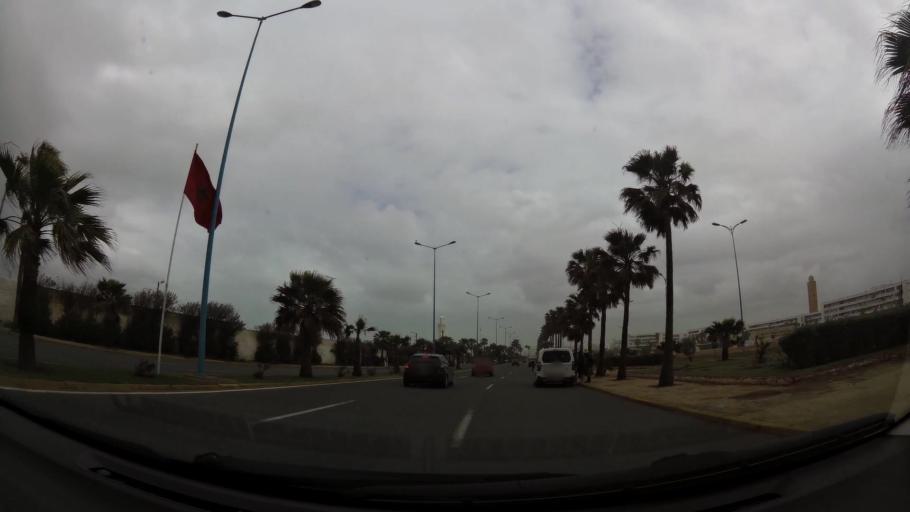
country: MA
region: Grand Casablanca
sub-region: Casablanca
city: Casablanca
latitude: 33.6072
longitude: -7.6546
